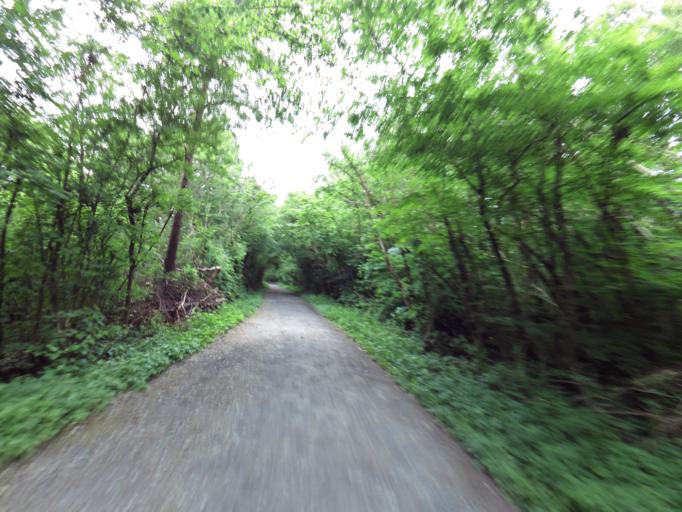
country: IE
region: Connaught
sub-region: County Galway
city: Gort
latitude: 53.0914
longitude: -8.8436
